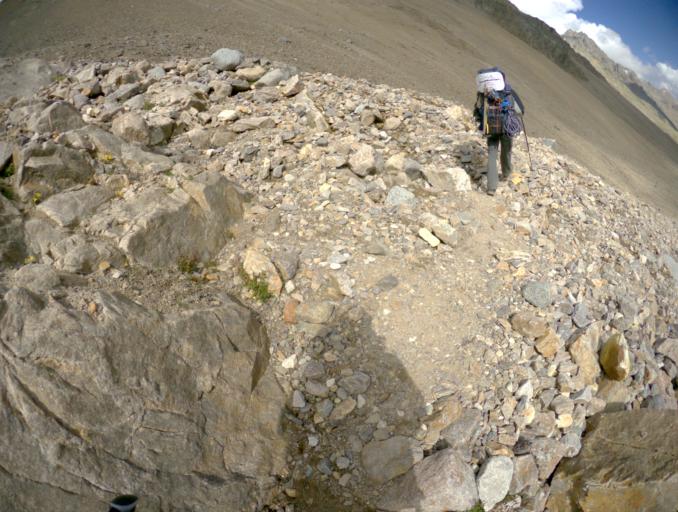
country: RU
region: Kabardino-Balkariya
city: Terskol
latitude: 43.3350
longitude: 42.5541
